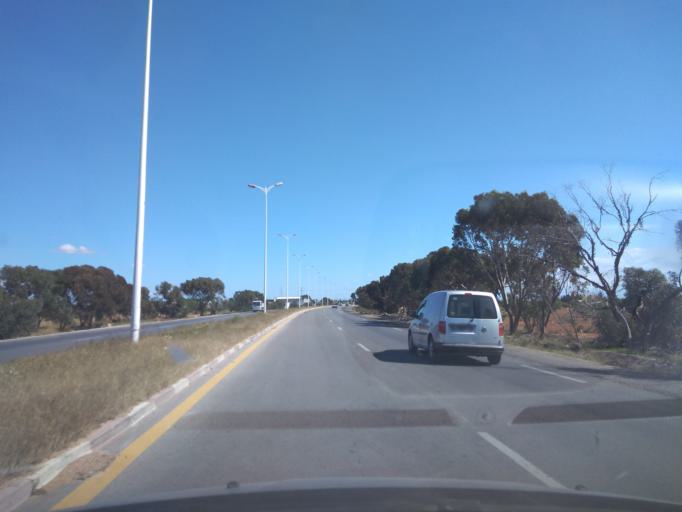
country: TN
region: Safaqis
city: Sfax
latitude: 34.8262
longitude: 10.7171
